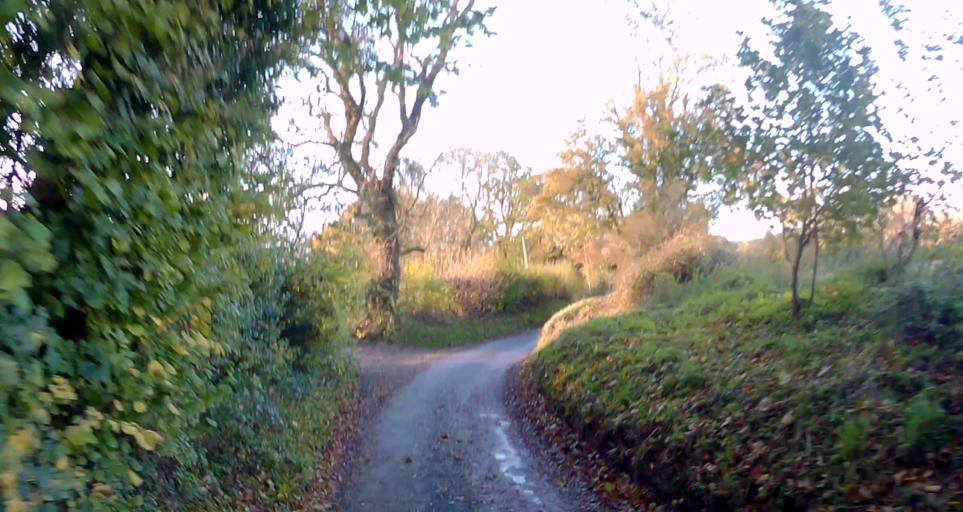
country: GB
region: England
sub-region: Hampshire
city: Basingstoke
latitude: 51.2075
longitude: -1.0827
